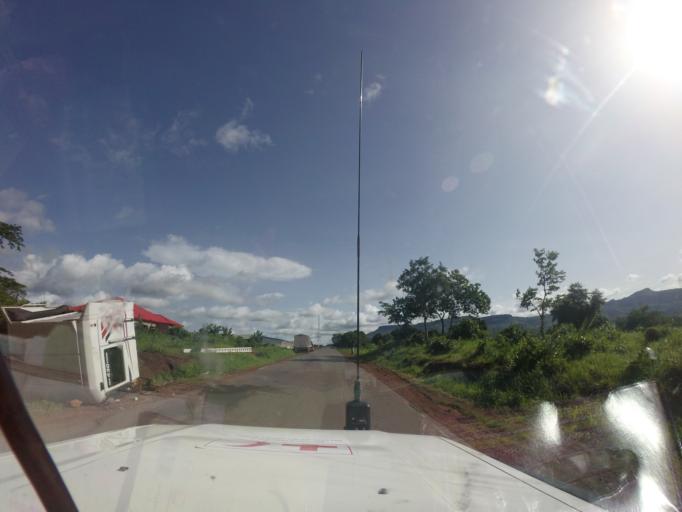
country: GN
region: Mamou
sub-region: Mamou Prefecture
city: Mamou
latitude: 10.2635
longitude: -12.4535
